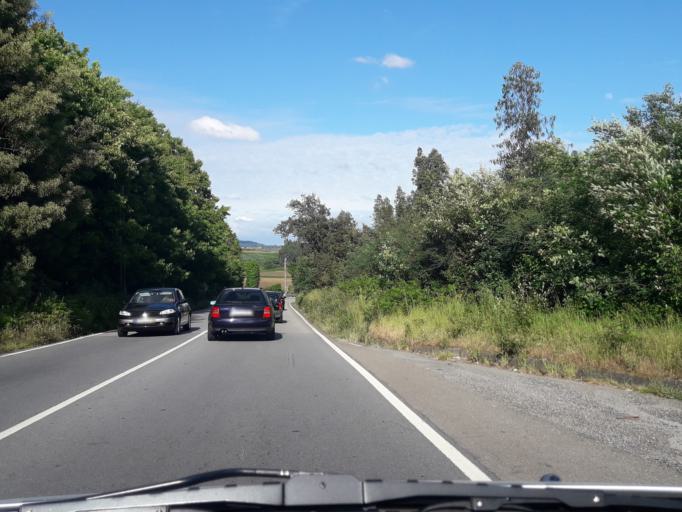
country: PT
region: Braga
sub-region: Vila Nova de Famalicao
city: Vila Nova de Famalicao
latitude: 41.3886
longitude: -8.5084
